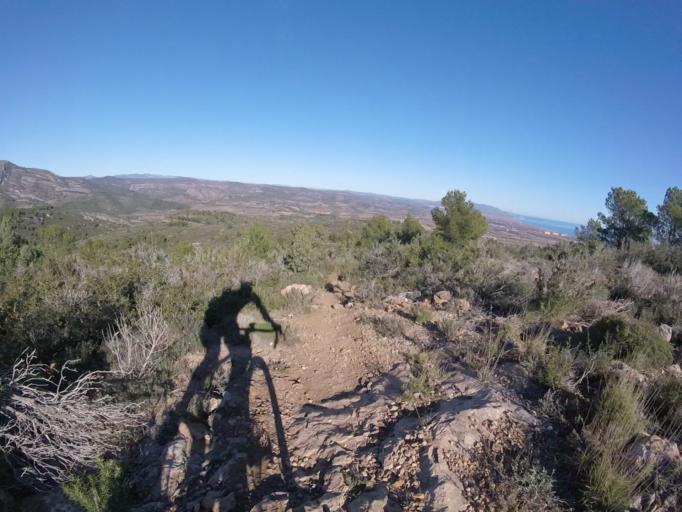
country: ES
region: Valencia
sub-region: Provincia de Castello
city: Orpesa/Oropesa del Mar
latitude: 40.1089
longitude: 0.1191
